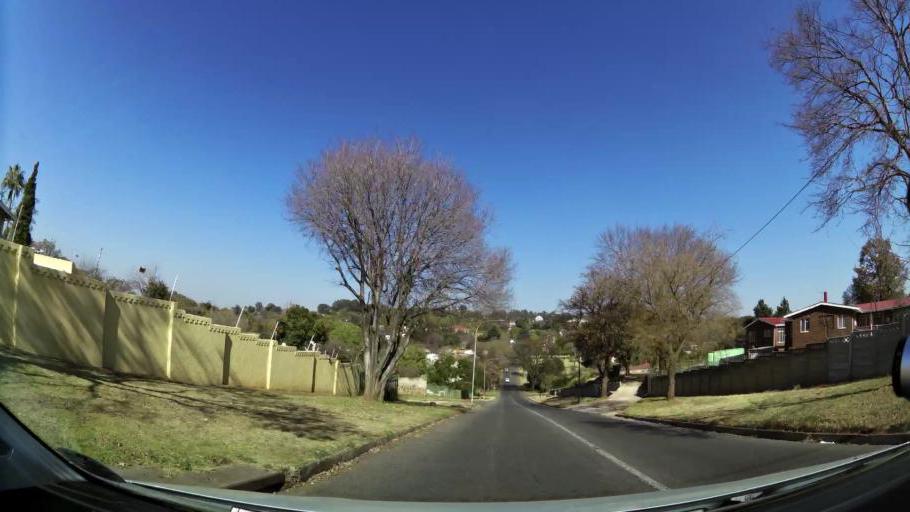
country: ZA
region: Gauteng
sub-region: City of Johannesburg Metropolitan Municipality
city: Johannesburg
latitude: -26.1769
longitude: 28.0751
